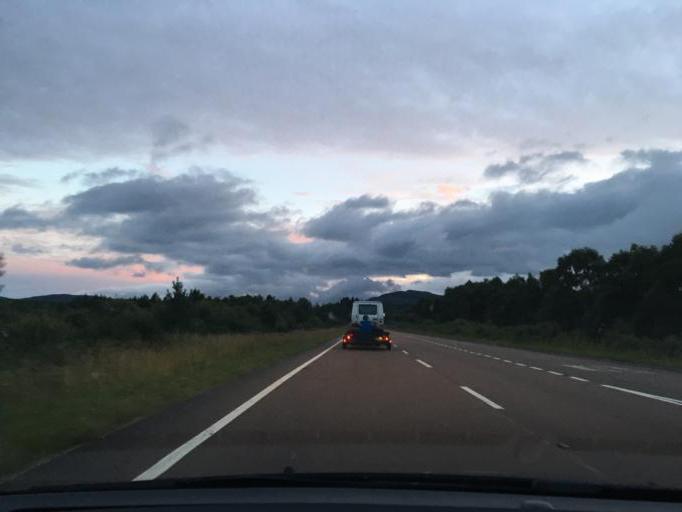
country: GB
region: Scotland
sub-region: Highland
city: Kingussie
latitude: 57.0386
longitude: -4.1513
